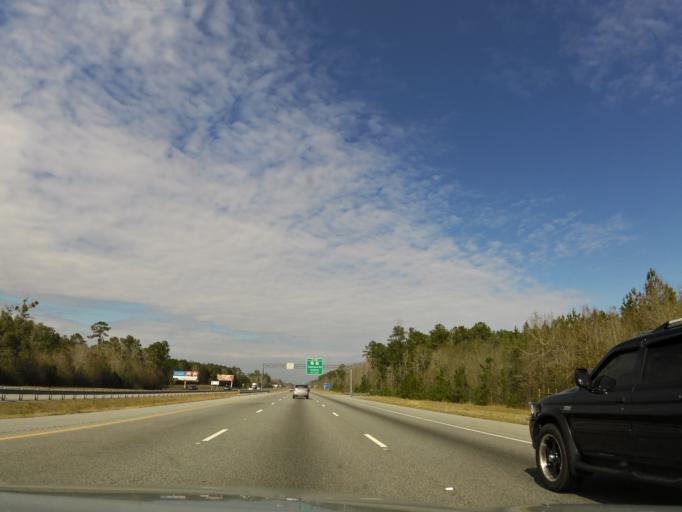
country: US
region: Georgia
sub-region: McIntosh County
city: Darien
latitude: 31.5114
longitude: -81.4459
